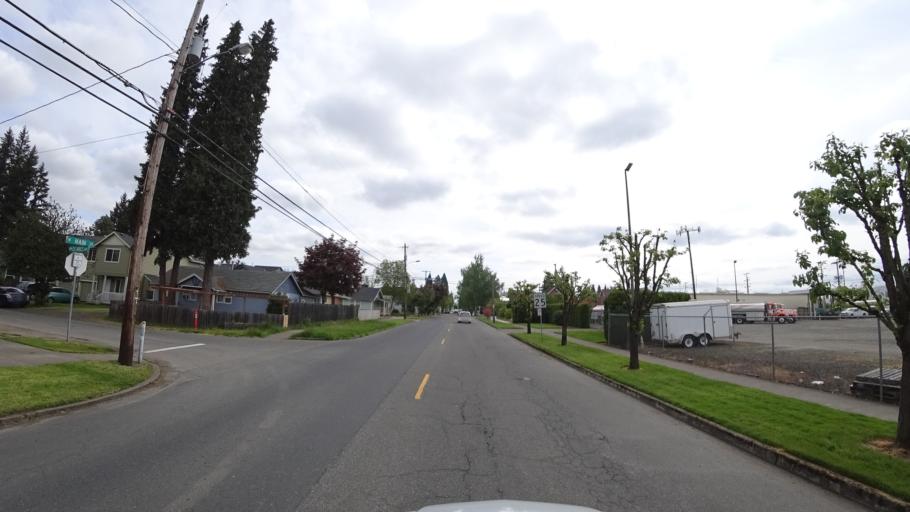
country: US
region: Oregon
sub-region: Washington County
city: Hillsboro
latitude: 45.5227
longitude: -122.9954
